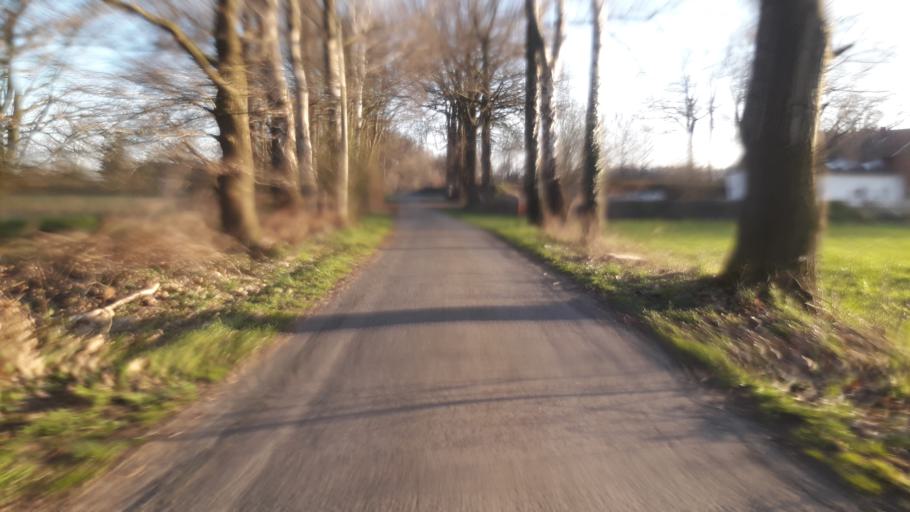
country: DE
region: North Rhine-Westphalia
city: Rietberg
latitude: 51.7866
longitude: 8.4544
